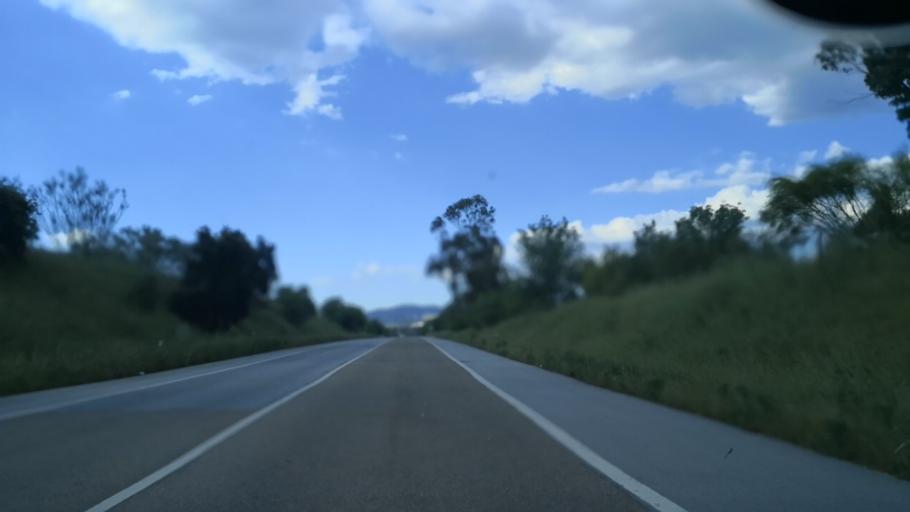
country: PT
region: Portalegre
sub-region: Portalegre
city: Urra
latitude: 39.2383
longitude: -7.4519
